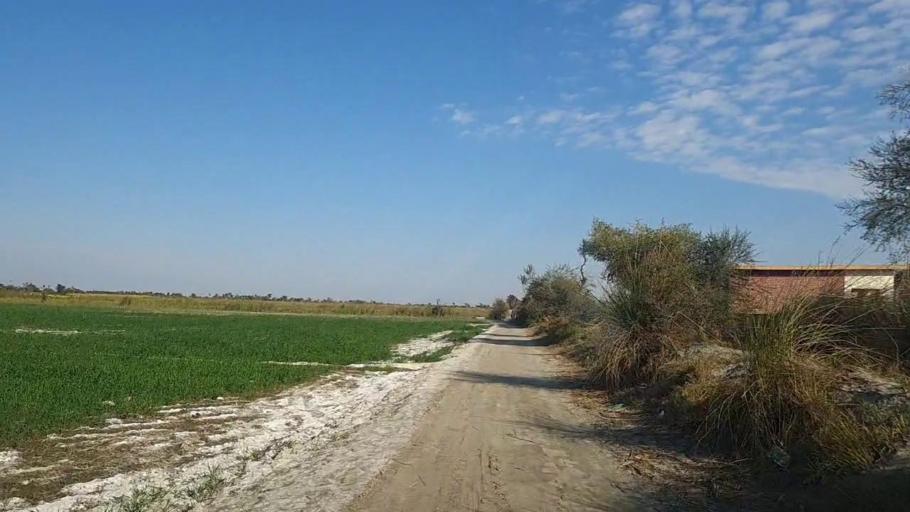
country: PK
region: Sindh
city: Khadro
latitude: 26.3024
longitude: 68.8302
